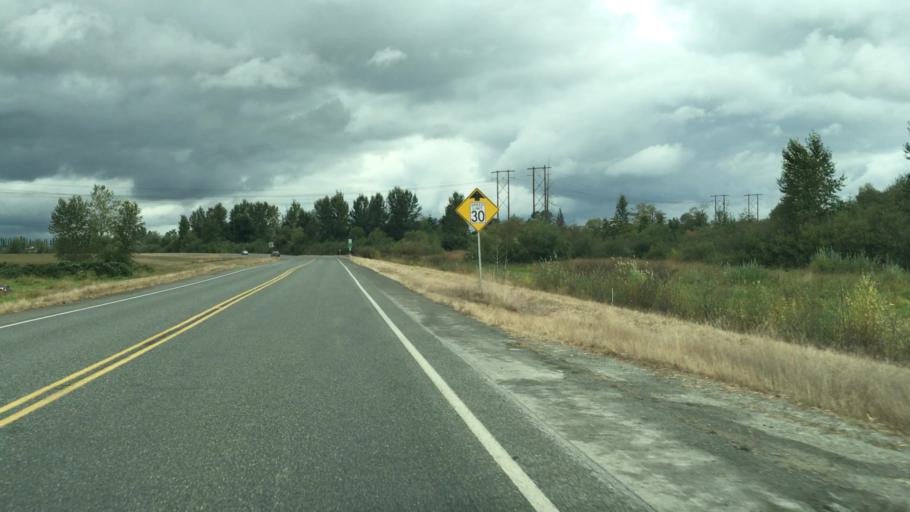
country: US
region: Washington
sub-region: Snohomish County
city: Everett
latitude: 47.9354
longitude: -122.1718
